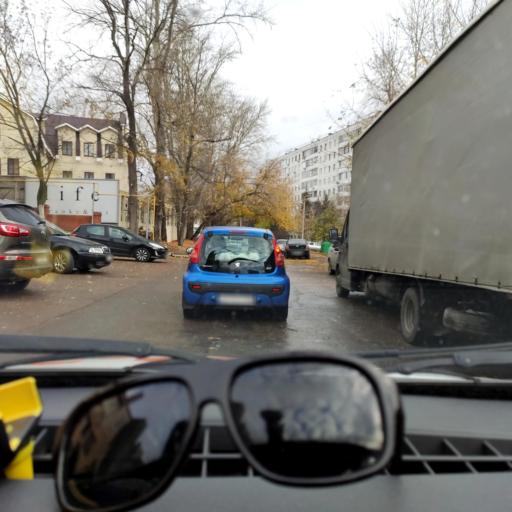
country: RU
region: Bashkortostan
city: Ufa
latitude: 54.7379
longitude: 55.9958
